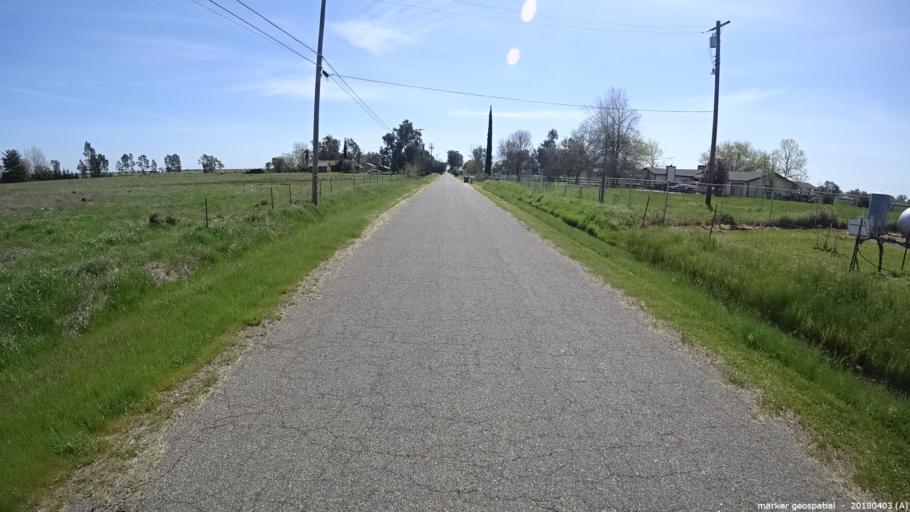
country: US
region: California
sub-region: Sacramento County
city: Clay
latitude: 38.3494
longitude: -121.2146
